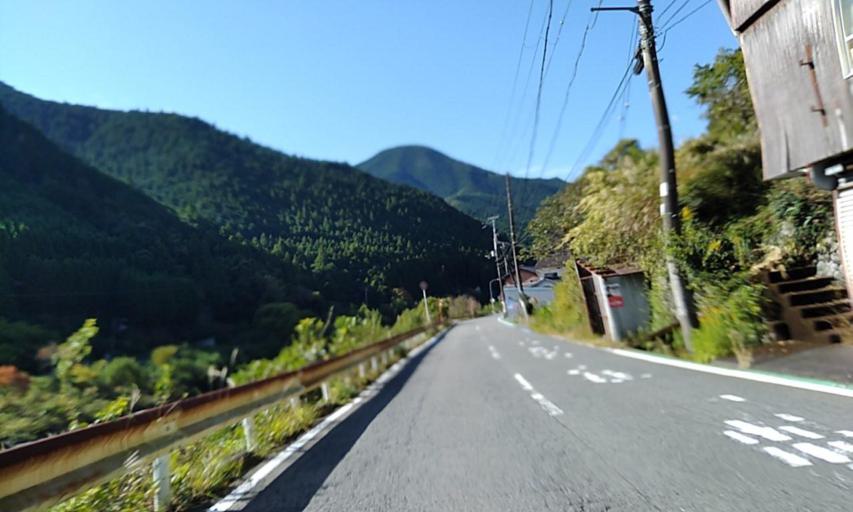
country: JP
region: Wakayama
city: Kainan
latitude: 34.0516
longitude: 135.3549
